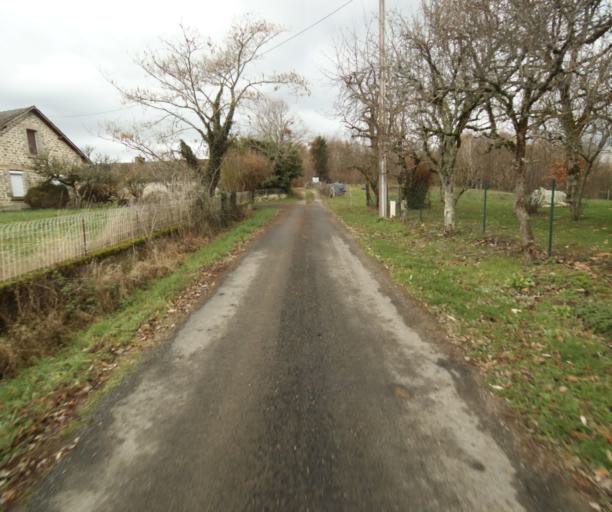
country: FR
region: Limousin
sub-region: Departement de la Correze
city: Saint-Mexant
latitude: 45.2876
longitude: 1.6300
